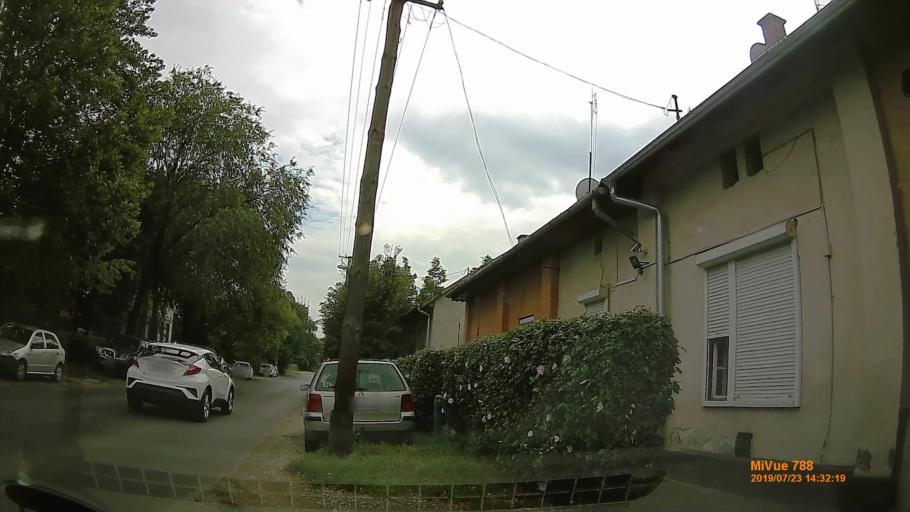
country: HU
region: Szabolcs-Szatmar-Bereg
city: Nyiregyhaza
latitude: 47.9405
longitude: 21.7130
